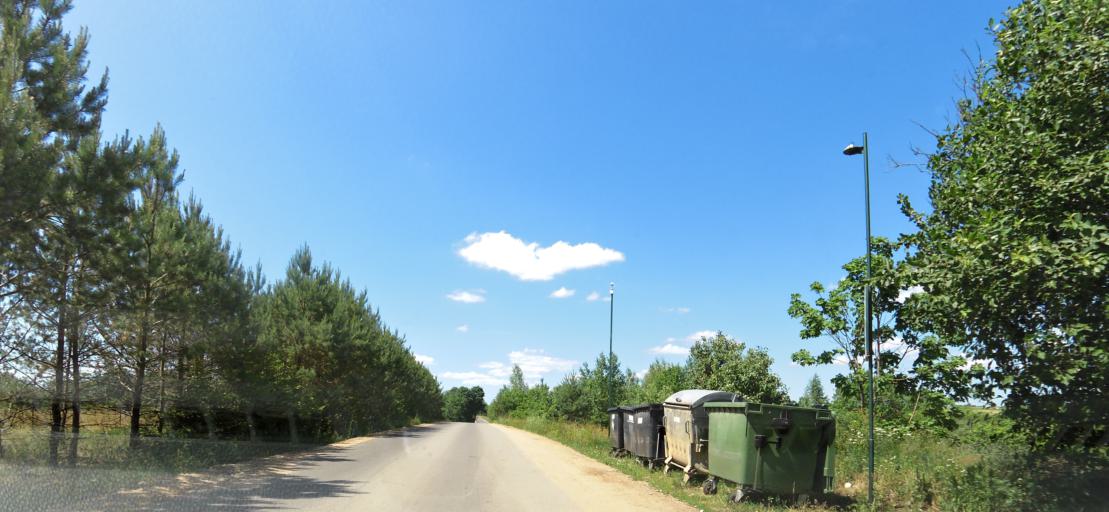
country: LT
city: Nemencine
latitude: 54.8733
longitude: 25.5496
